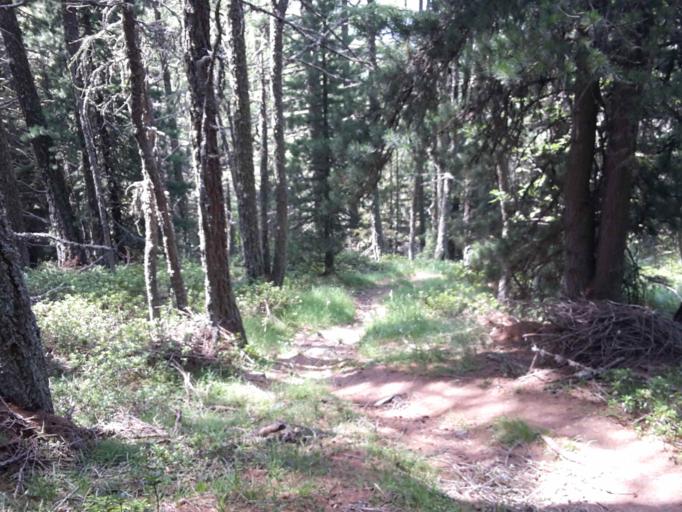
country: IT
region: Aosta Valley
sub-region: Valle d'Aosta
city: Brusson
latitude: 45.7485
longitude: 7.7161
